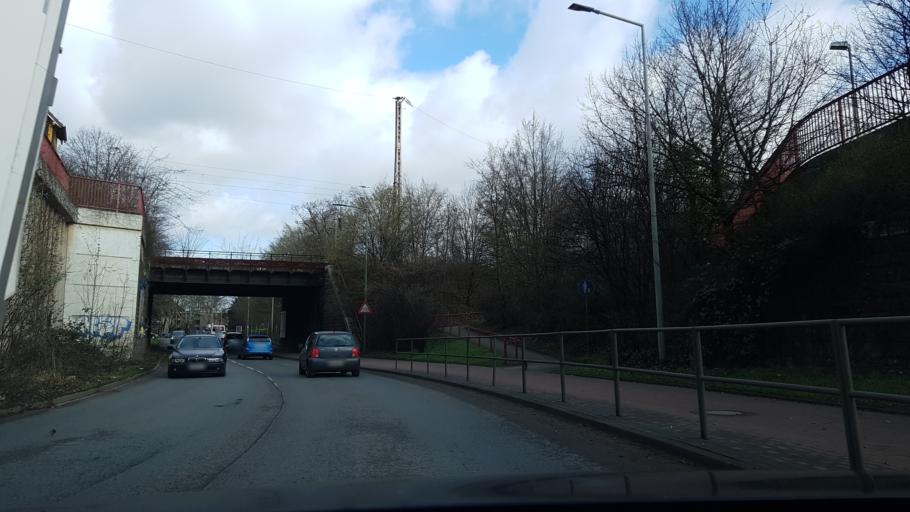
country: DE
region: North Rhine-Westphalia
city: Meiderich
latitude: 51.4603
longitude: 6.7974
